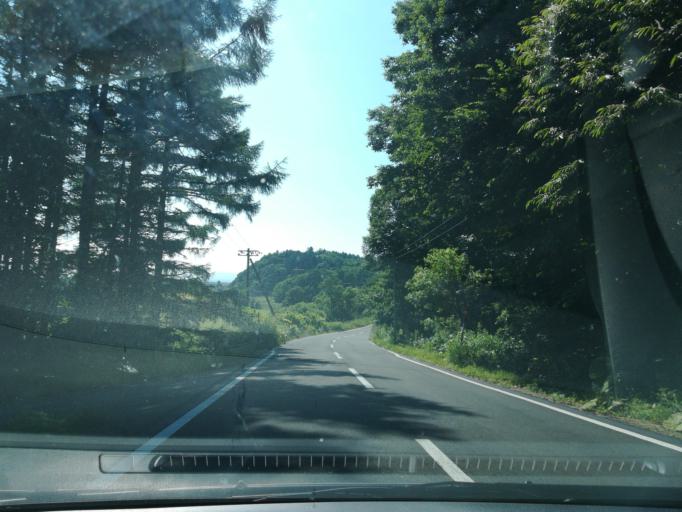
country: JP
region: Hokkaido
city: Chitose
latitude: 42.9105
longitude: 141.7316
